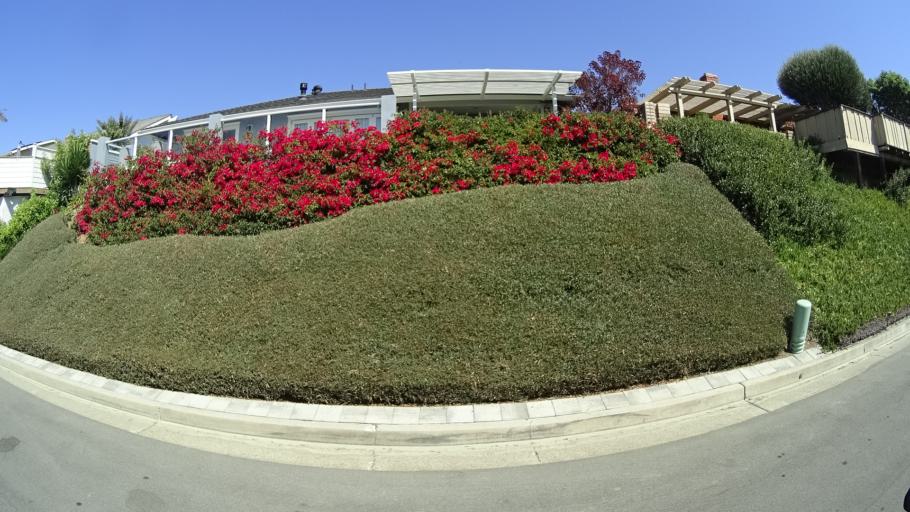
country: US
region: California
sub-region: Orange County
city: San Clemente
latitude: 33.4455
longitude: -117.6411
